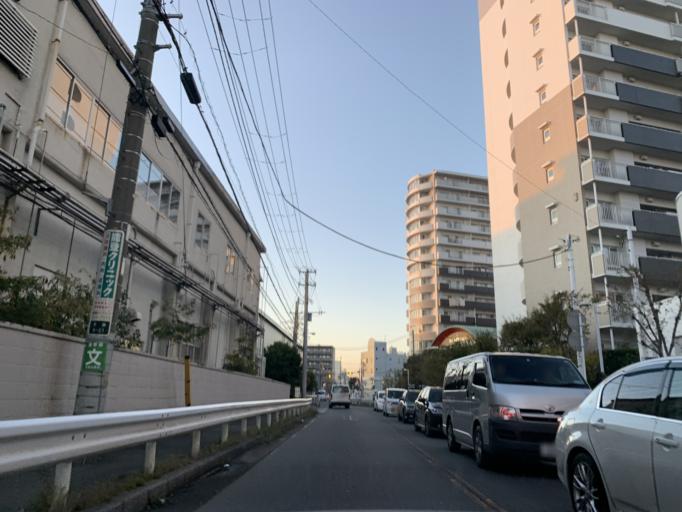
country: JP
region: Tokyo
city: Urayasu
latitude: 35.7228
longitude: 139.9051
